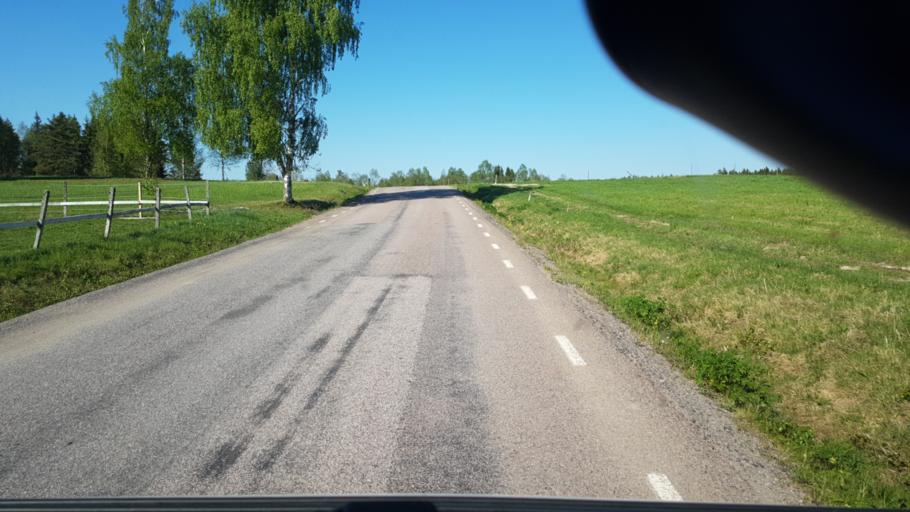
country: SE
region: Vaermland
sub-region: Eda Kommun
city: Charlottenberg
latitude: 59.8720
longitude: 12.3484
